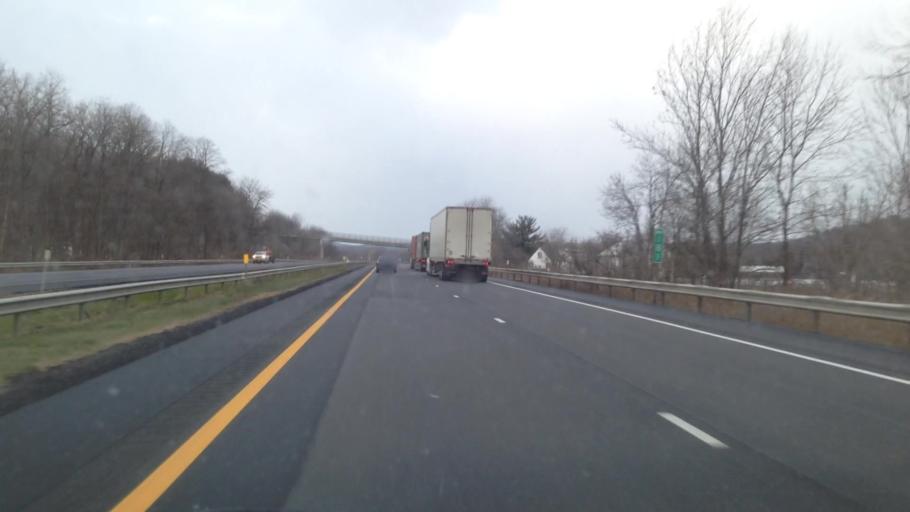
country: US
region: New York
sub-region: Montgomery County
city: Fonda
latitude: 42.9391
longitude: -74.3382
